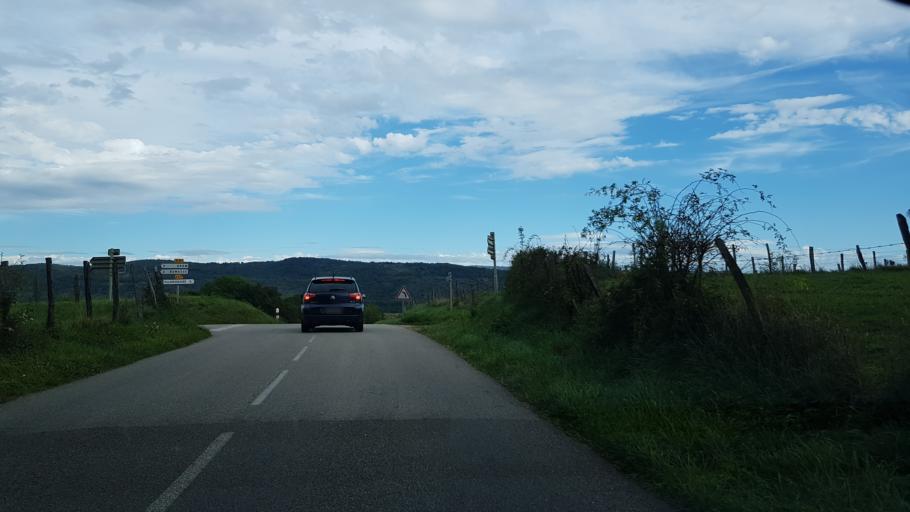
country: FR
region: Rhone-Alpes
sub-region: Departement de l'Ain
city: Villereversure
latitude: 46.1803
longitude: 5.3757
